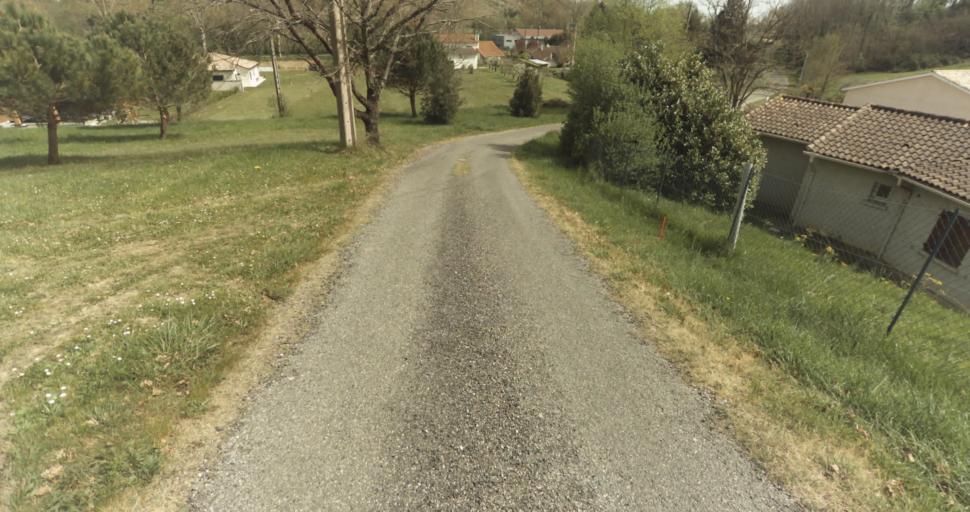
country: FR
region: Midi-Pyrenees
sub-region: Departement du Tarn-et-Garonne
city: Moissac
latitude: 44.1204
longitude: 1.1012
